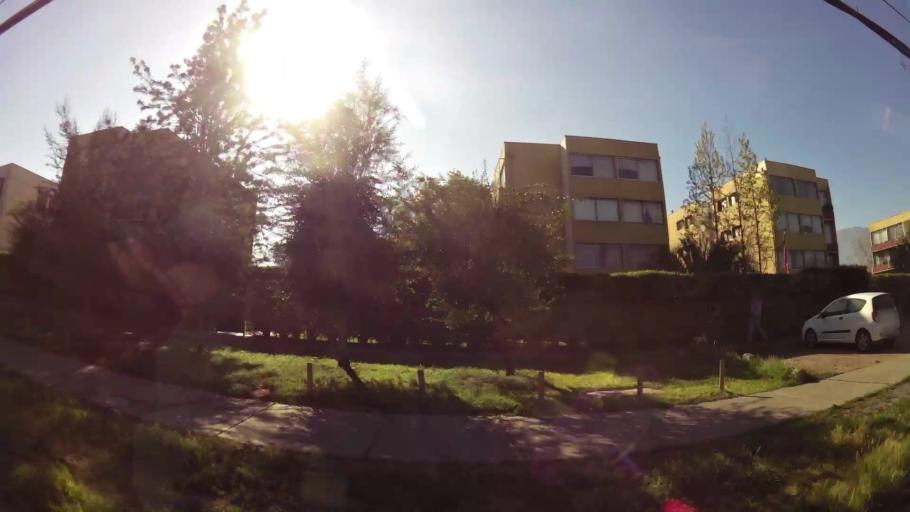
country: CL
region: Santiago Metropolitan
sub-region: Provincia de Santiago
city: Villa Presidente Frei, Nunoa, Santiago, Chile
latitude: -33.4502
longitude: -70.5513
